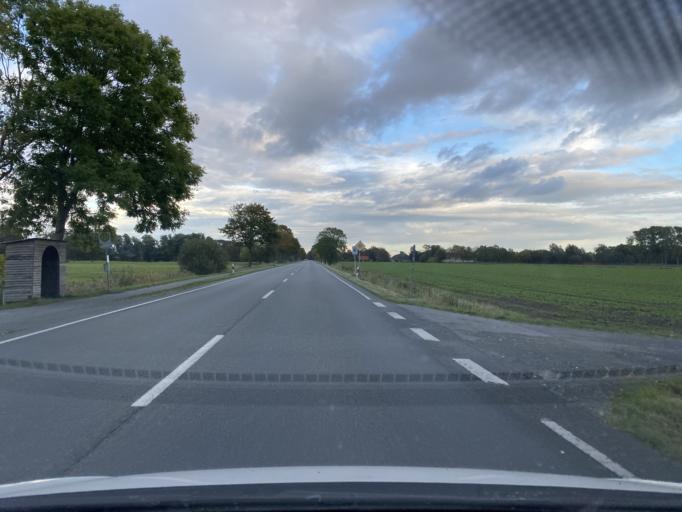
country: DE
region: Lower Saxony
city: Nordleda
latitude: 53.7997
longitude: 8.8474
